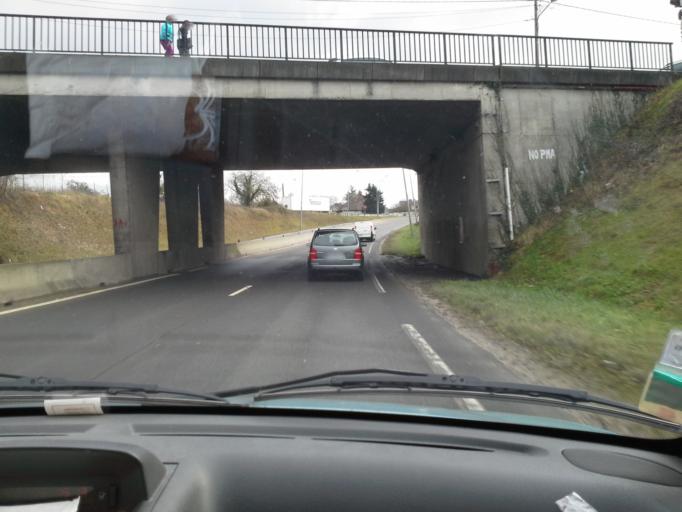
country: FR
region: Centre
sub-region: Departement du Loir-et-Cher
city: La Chaussee-Saint-Victor
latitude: 47.6026
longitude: 1.3485
